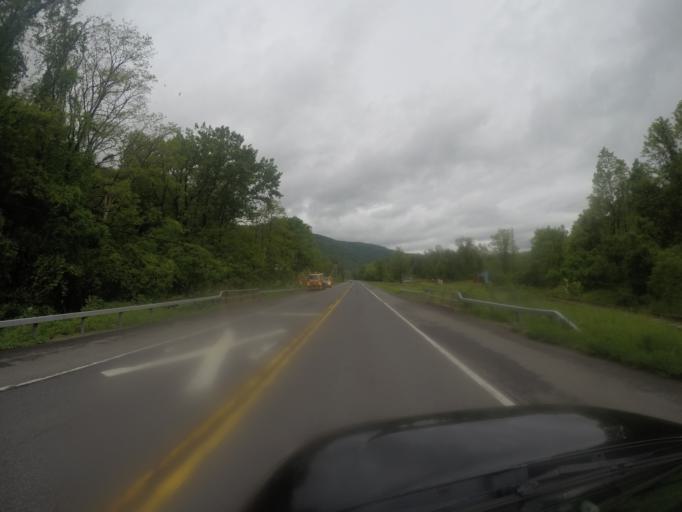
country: US
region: New York
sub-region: Ulster County
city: Shokan
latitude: 42.0534
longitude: -74.2932
